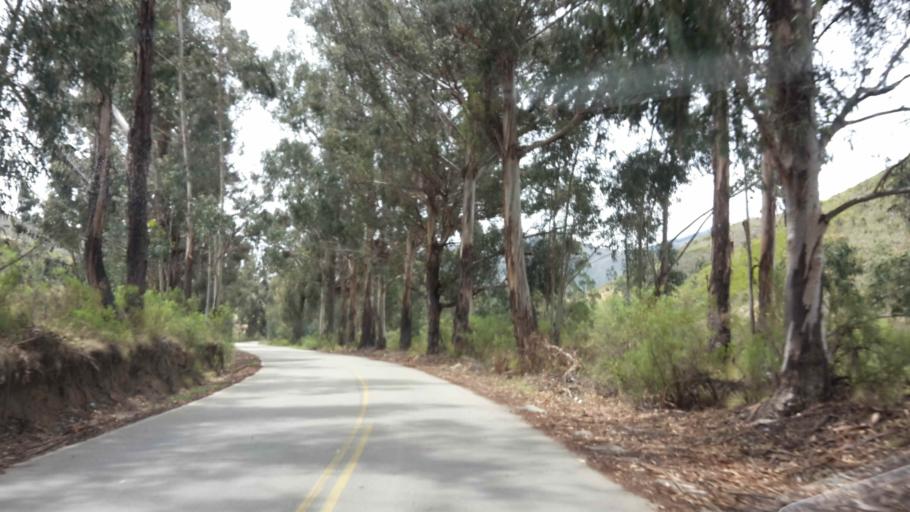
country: BO
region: Cochabamba
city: Totora
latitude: -17.6645
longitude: -65.2245
